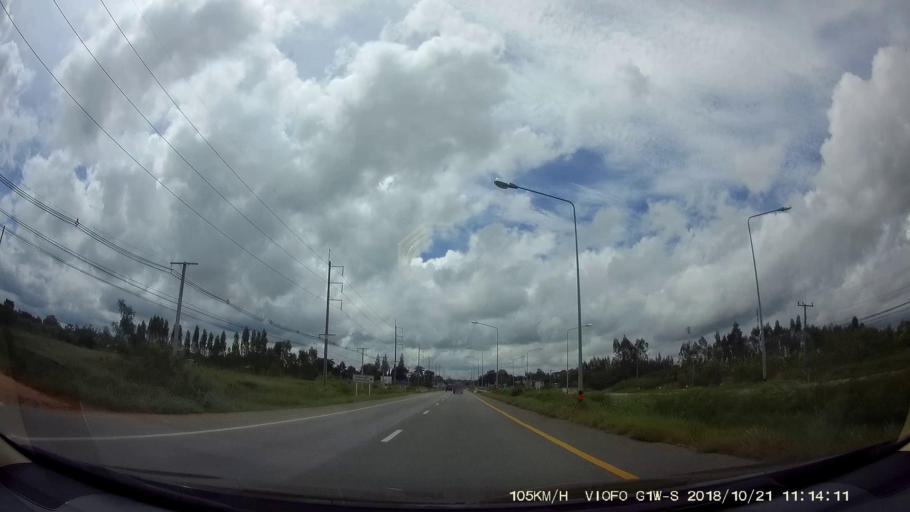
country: TH
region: Chaiyaphum
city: Chaiyaphum
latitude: 15.9073
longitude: 102.1249
